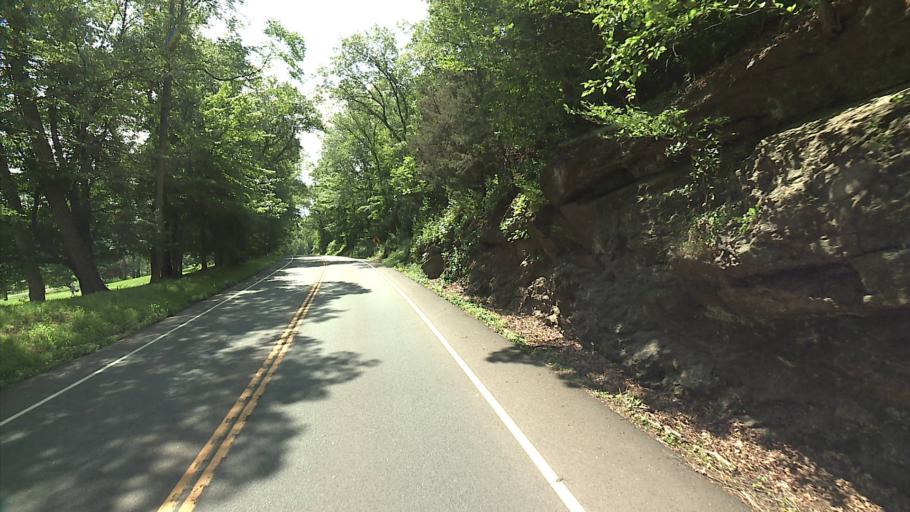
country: US
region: Connecticut
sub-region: Middlesex County
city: Portland
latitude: 41.5872
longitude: -72.6121
